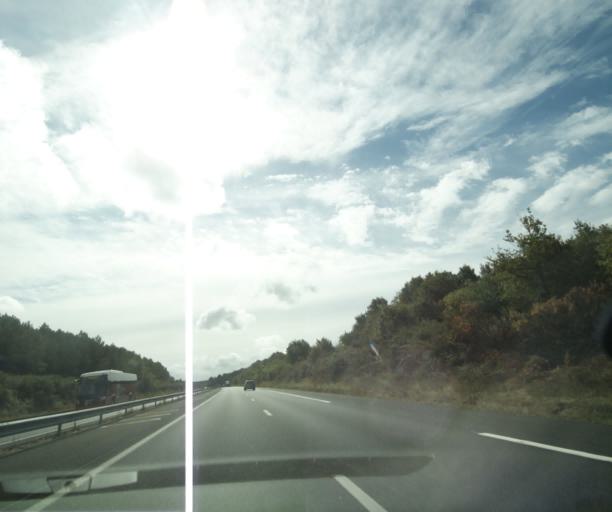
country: FR
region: Poitou-Charentes
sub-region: Departement de la Charente-Maritime
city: Thenac
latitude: 45.6439
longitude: -0.6291
